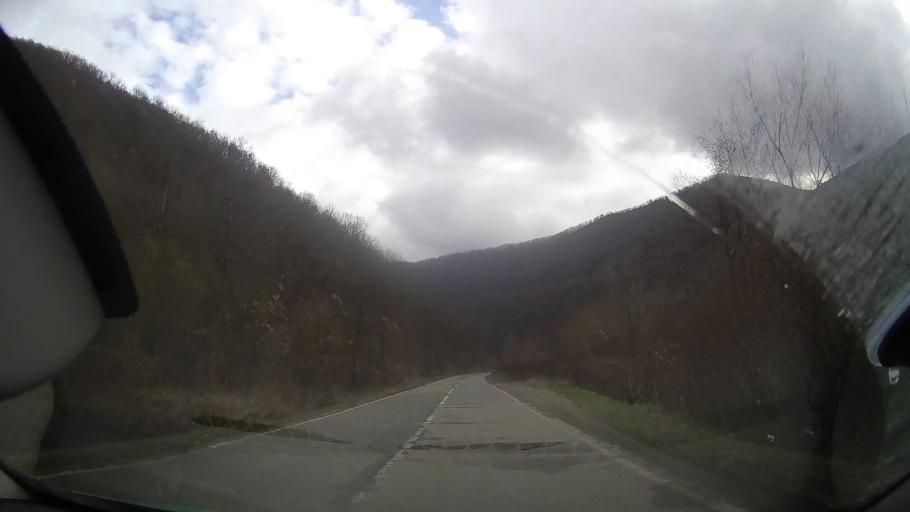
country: RO
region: Alba
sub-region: Comuna Rimetea
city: Rimetea
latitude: 46.5073
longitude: 23.5714
